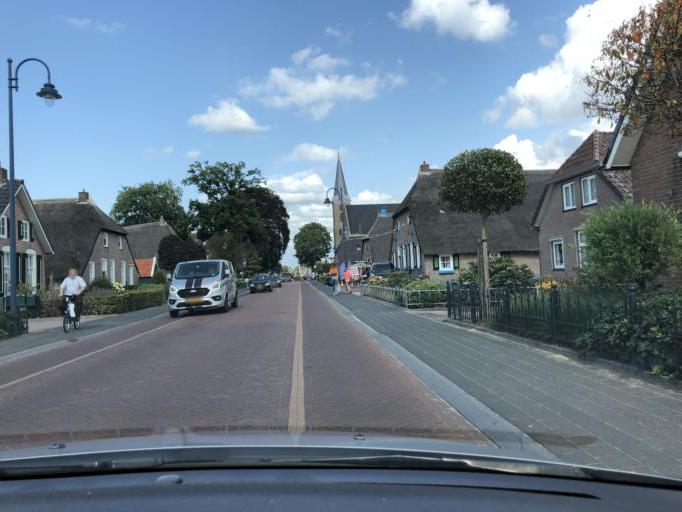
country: NL
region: Overijssel
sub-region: Gemeente Staphorst
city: Staphorst
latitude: 52.6448
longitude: 6.2054
